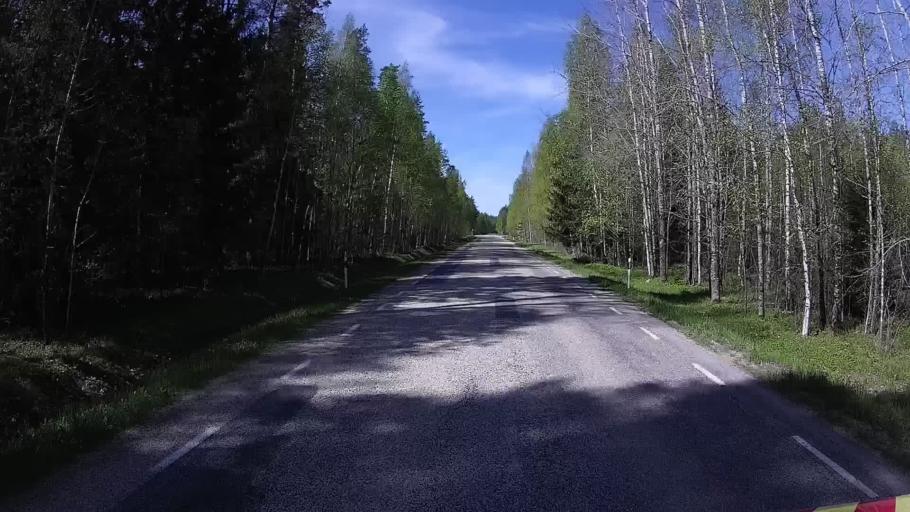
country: EE
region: Polvamaa
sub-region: Raepina vald
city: Rapina
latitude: 57.9645
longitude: 27.4895
